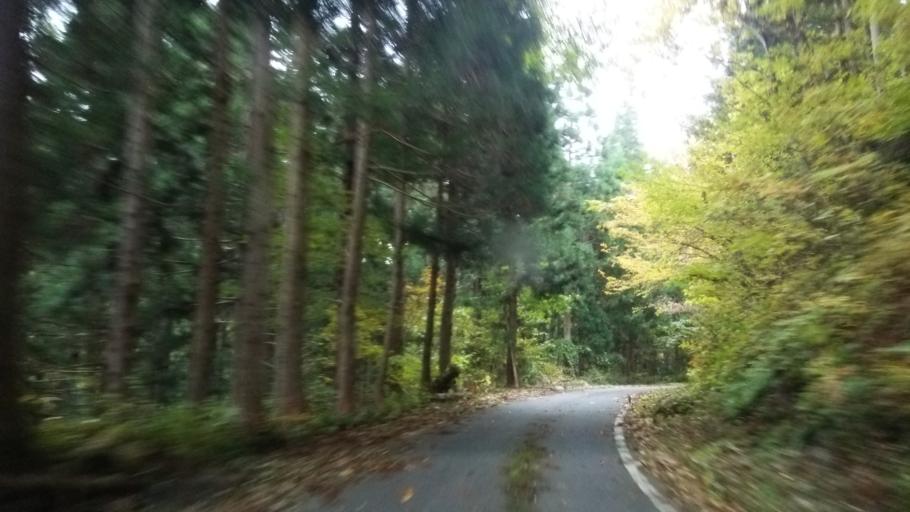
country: JP
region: Fukushima
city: Kitakata
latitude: 37.4065
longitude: 139.7059
